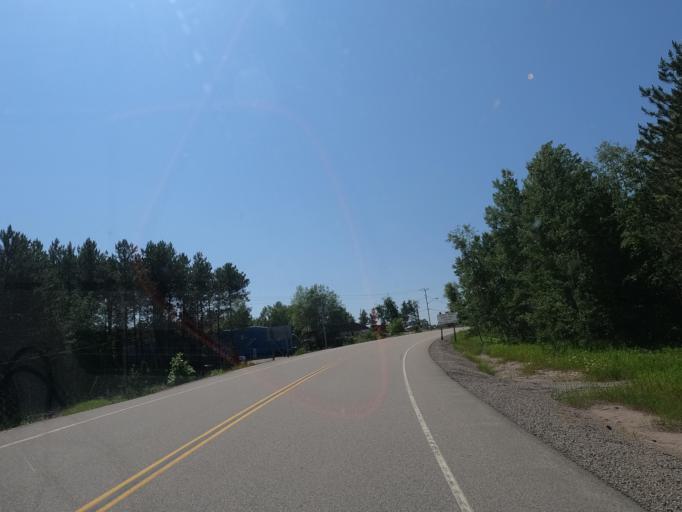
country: CA
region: Ontario
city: Dryden
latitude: 49.8552
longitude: -93.3632
